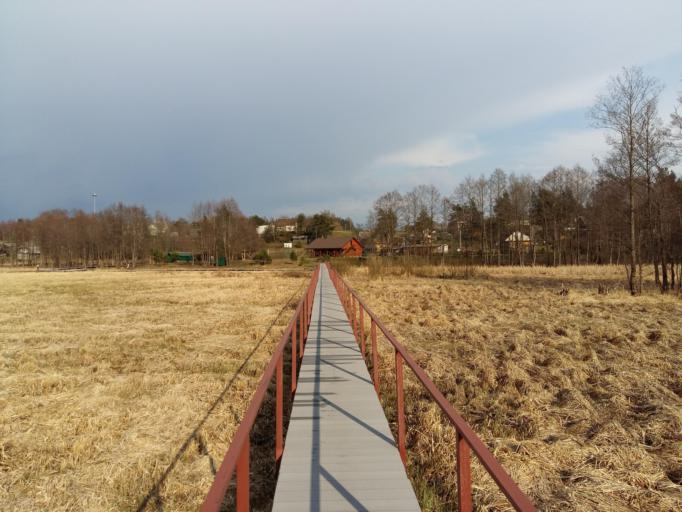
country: LT
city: Svencioneliai
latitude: 55.1568
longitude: 25.9851
